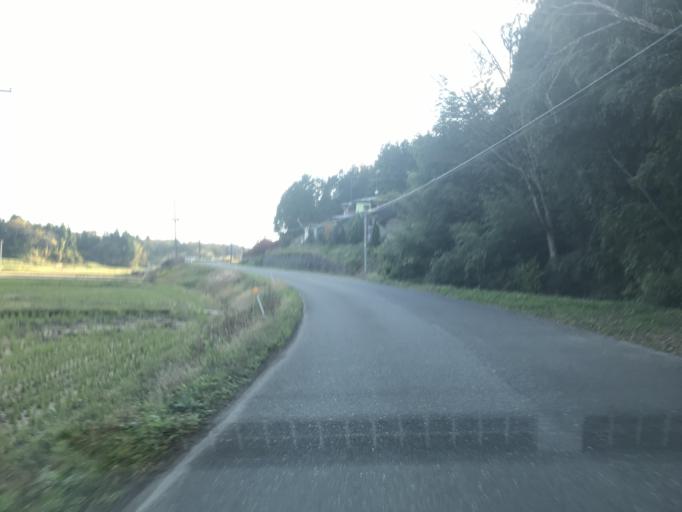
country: JP
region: Iwate
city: Ichinoseki
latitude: 38.8651
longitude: 141.1660
